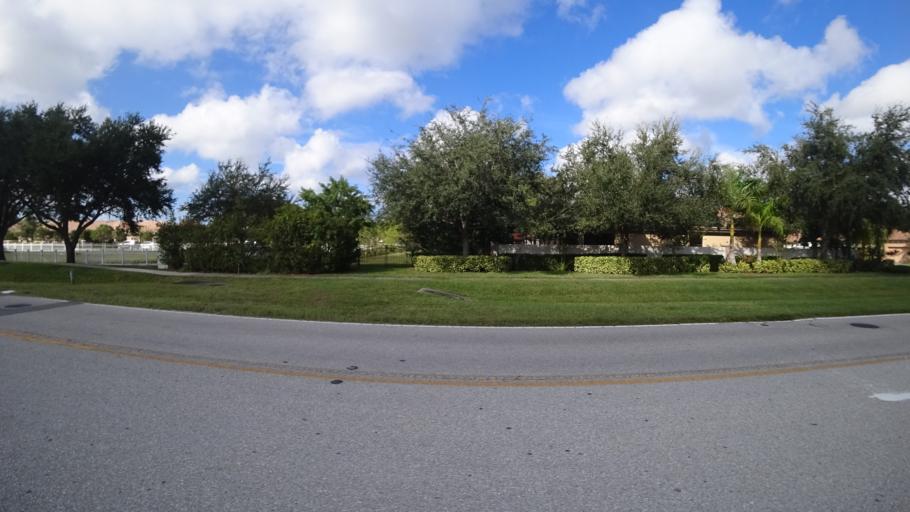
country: US
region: Florida
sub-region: Sarasota County
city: North Sarasota
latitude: 27.3961
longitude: -82.5136
